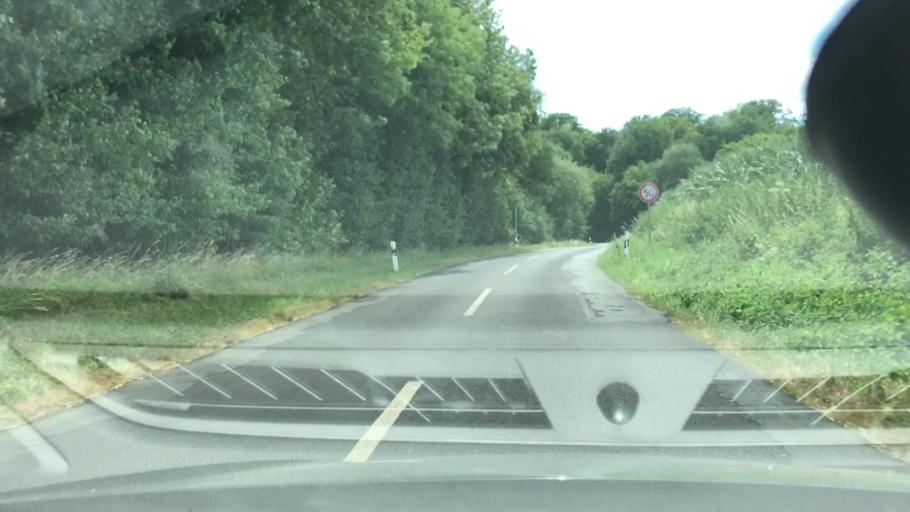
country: DE
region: Hesse
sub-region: Regierungsbezirk Darmstadt
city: Langenselbold
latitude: 50.1982
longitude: 9.0294
